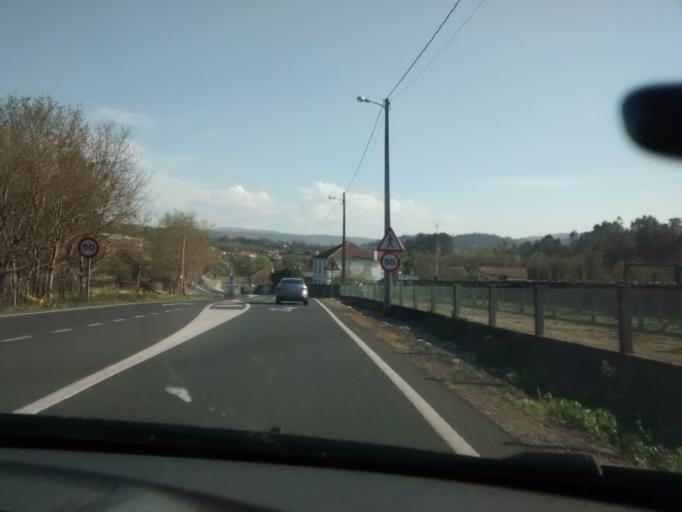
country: ES
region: Galicia
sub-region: Provincia da Coruna
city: Teo
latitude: 42.7673
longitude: -8.5492
